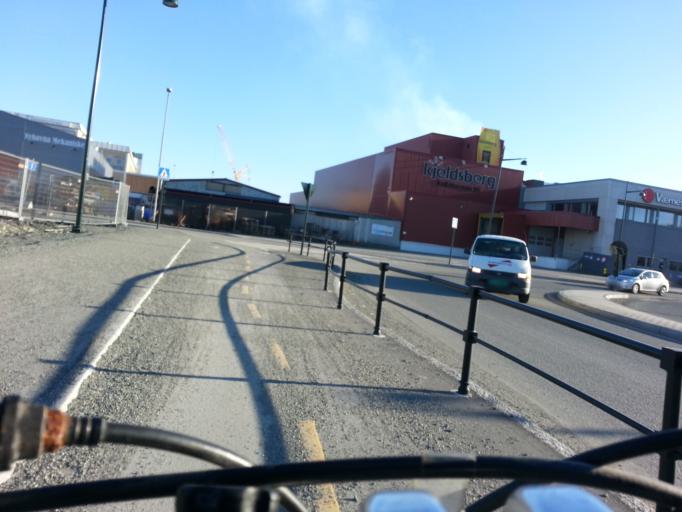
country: NO
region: Sor-Trondelag
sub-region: Trondheim
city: Trondheim
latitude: 63.4377
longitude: 10.4149
